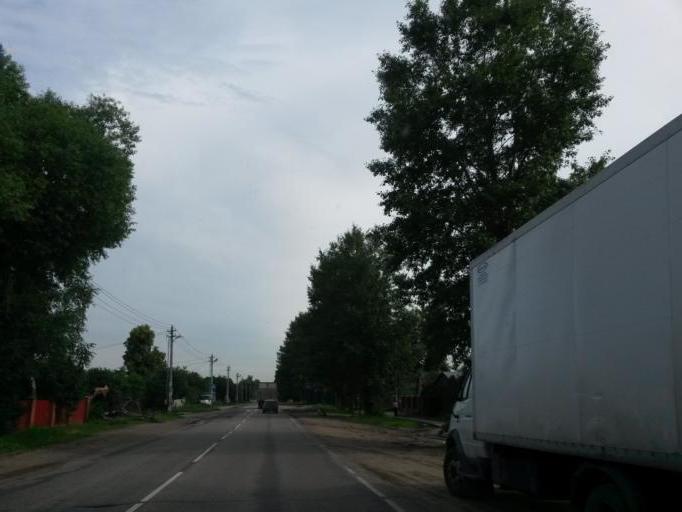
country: RU
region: Moskovskaya
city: Yam
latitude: 55.4812
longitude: 37.7514
